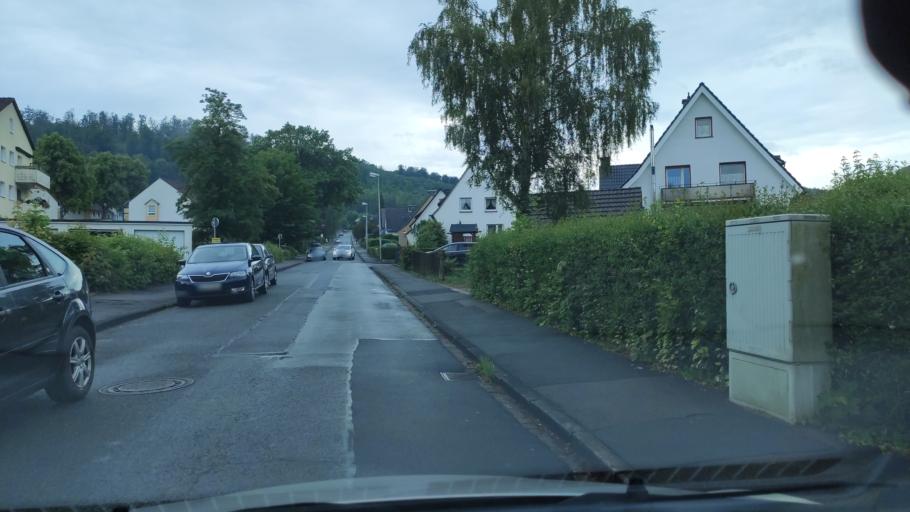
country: DE
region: North Rhine-Westphalia
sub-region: Regierungsbezirk Detmold
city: Hoexter
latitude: 51.7698
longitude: 9.3684
